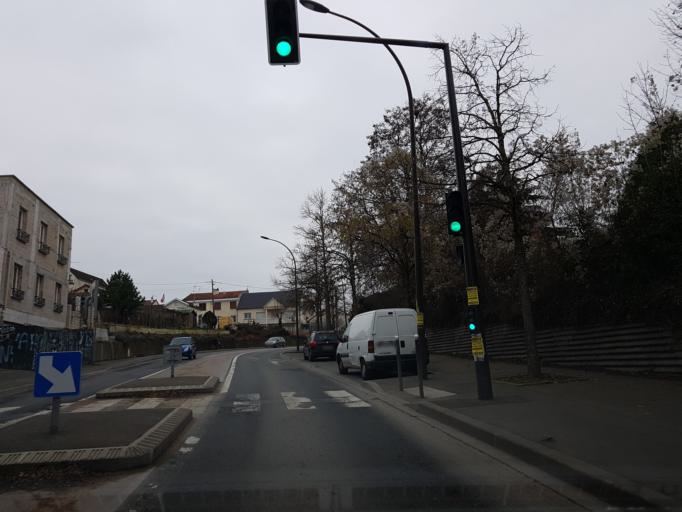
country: FR
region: Ile-de-France
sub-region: Departement du Val-de-Marne
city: Villejuif
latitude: 48.7891
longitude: 2.3782
